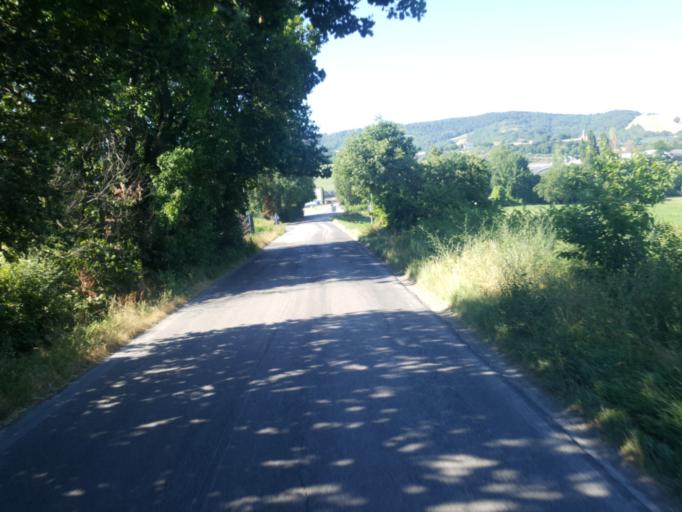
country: IT
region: The Marches
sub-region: Provincia di Pesaro e Urbino
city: Padiglione
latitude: 43.8380
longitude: 12.7175
